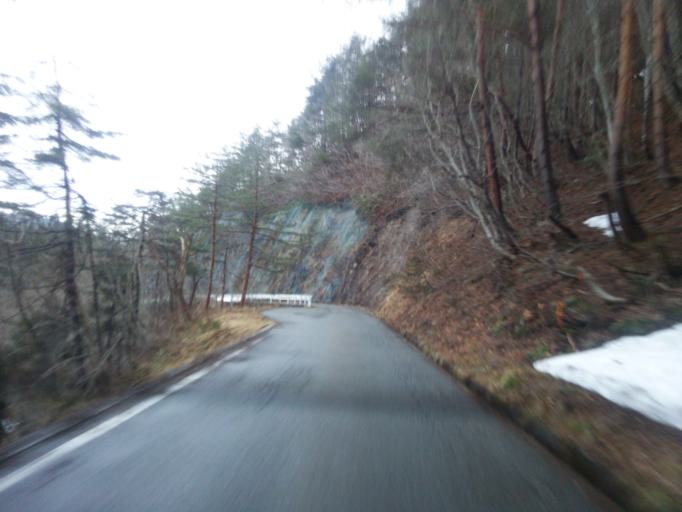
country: JP
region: Fukushima
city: Kitakata
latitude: 37.6888
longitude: 139.9363
